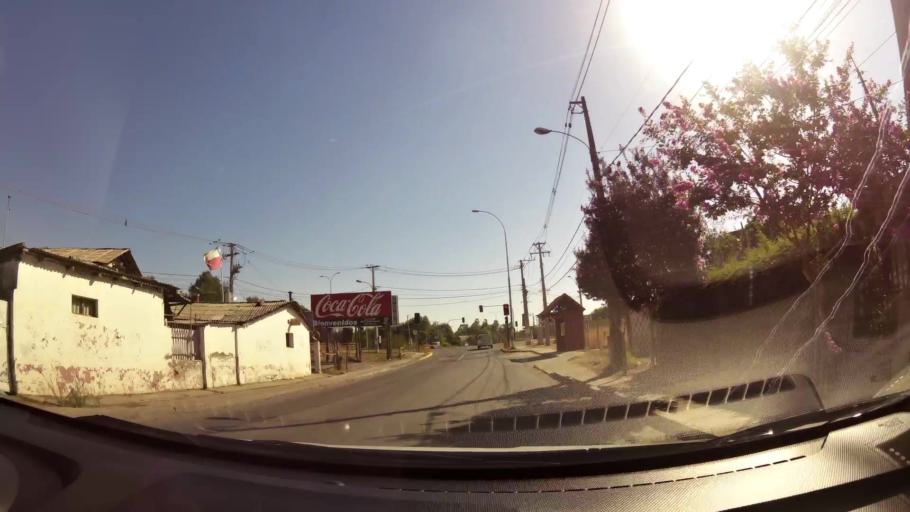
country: CL
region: Maule
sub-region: Provincia de Talca
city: Talca
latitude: -35.3991
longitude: -71.6272
